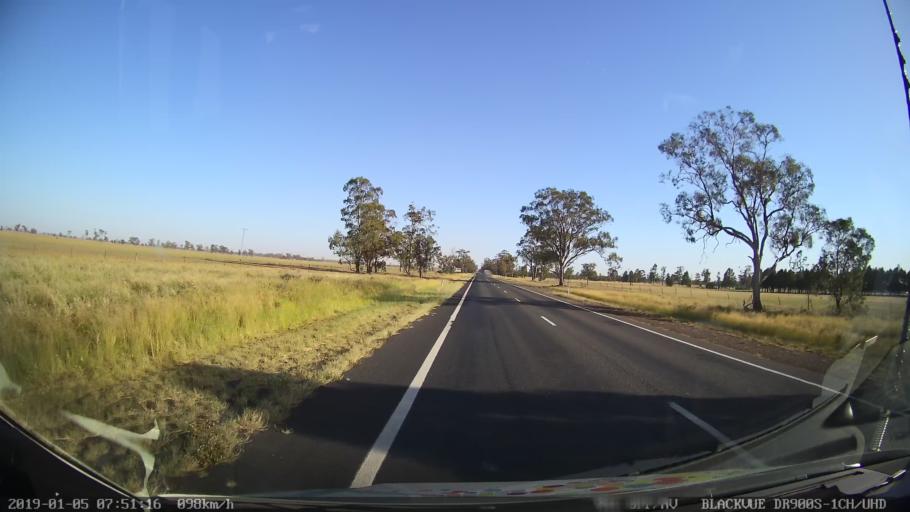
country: AU
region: New South Wales
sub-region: Gilgandra
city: Gilgandra
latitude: -31.7754
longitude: 148.6388
